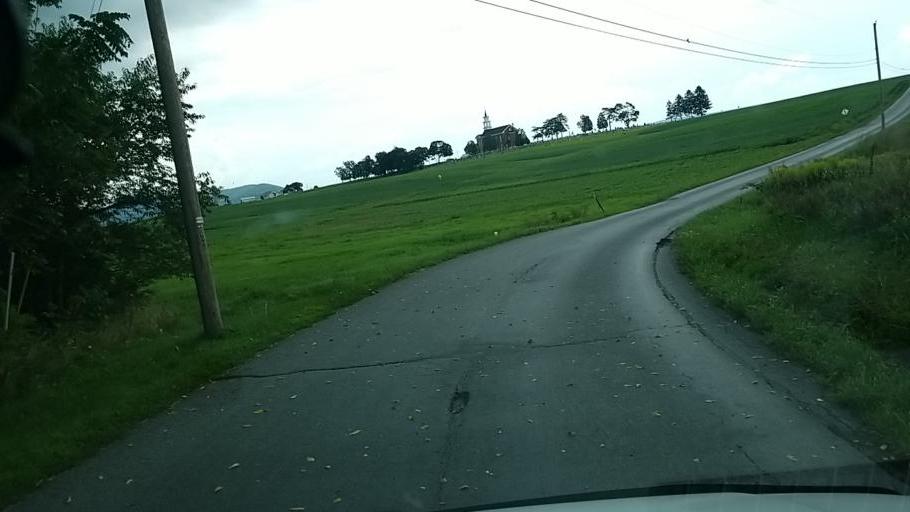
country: US
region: Pennsylvania
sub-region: Dauphin County
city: Elizabethville
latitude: 40.5897
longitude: -76.8223
